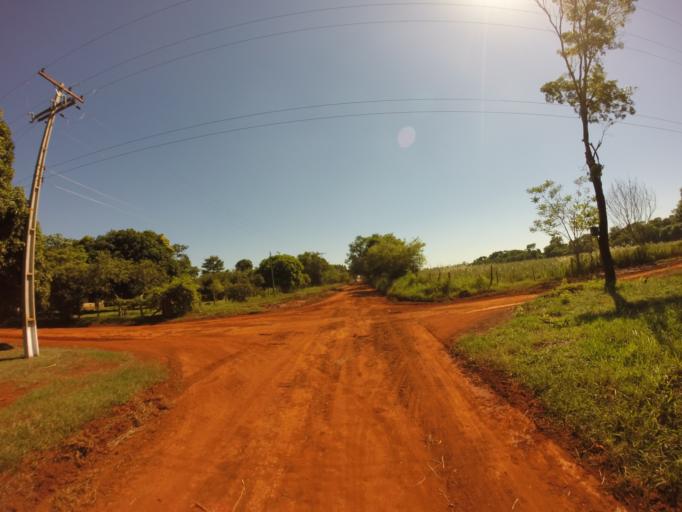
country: PY
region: Alto Parana
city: Ciudad del Este
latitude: -25.4320
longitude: -54.6615
